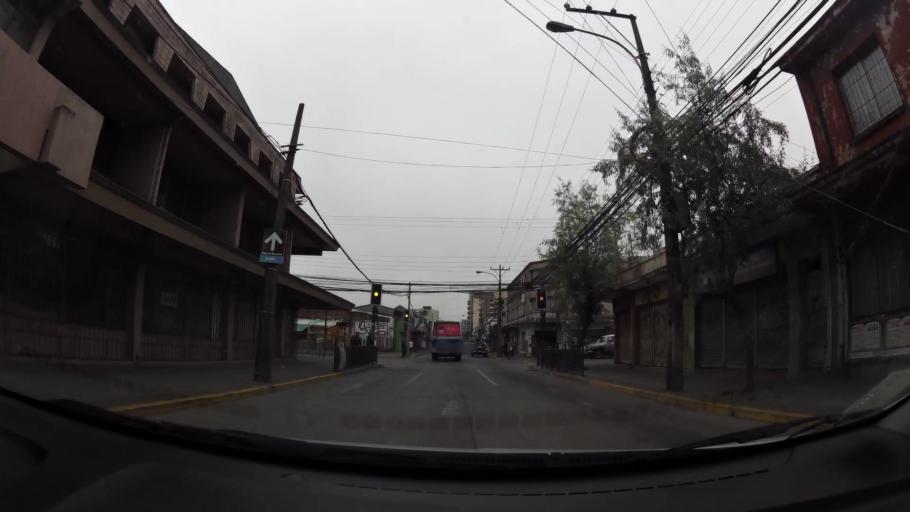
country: CL
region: Biobio
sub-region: Provincia de Concepcion
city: Concepcion
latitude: -36.8230
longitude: -73.0480
